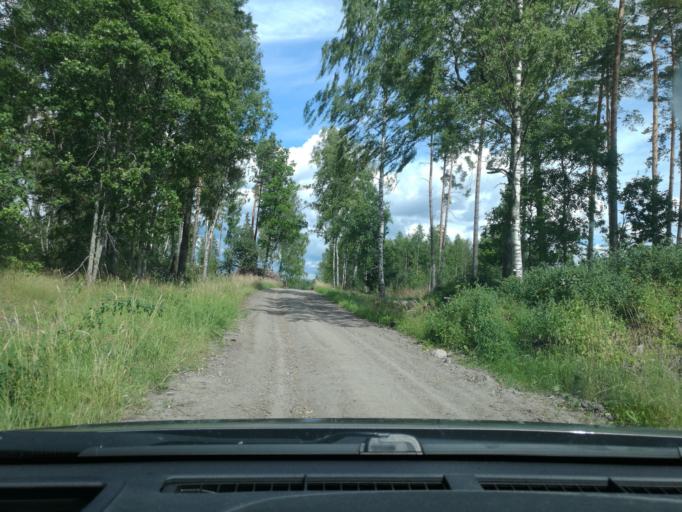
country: SE
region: Stockholm
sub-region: Sigtuna Kommun
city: Marsta
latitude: 59.6073
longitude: 17.8012
